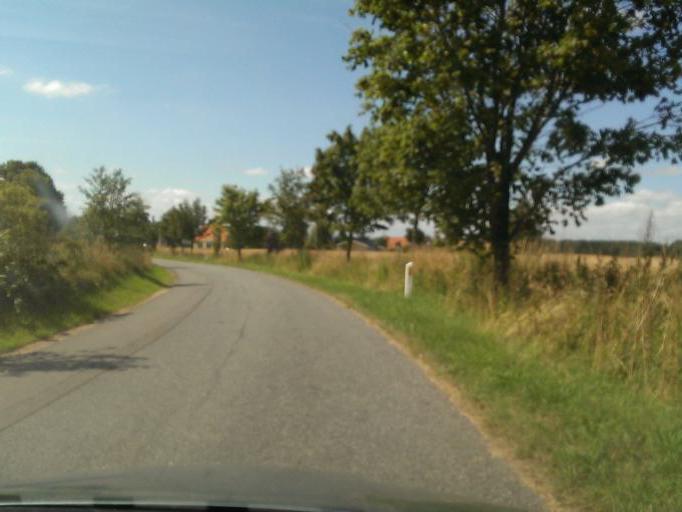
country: DK
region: Central Jutland
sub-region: Syddjurs Kommune
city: Ronde
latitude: 56.2695
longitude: 10.5612
